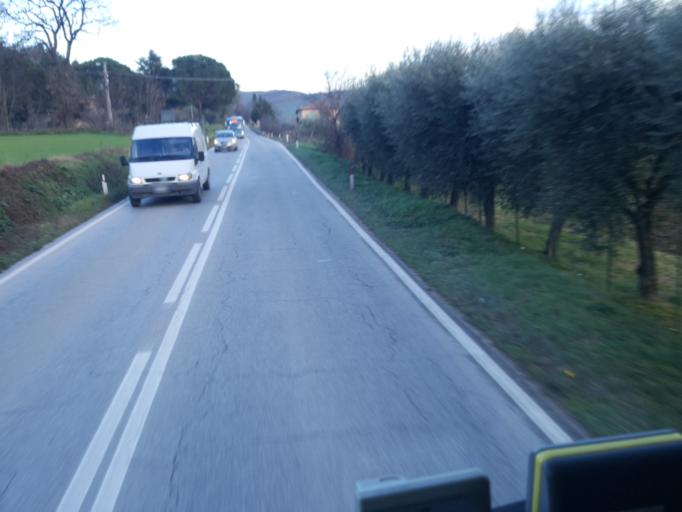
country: IT
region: The Marches
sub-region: Provincia di Macerata
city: San Severino Marche
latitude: 43.2367
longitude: 13.2014
